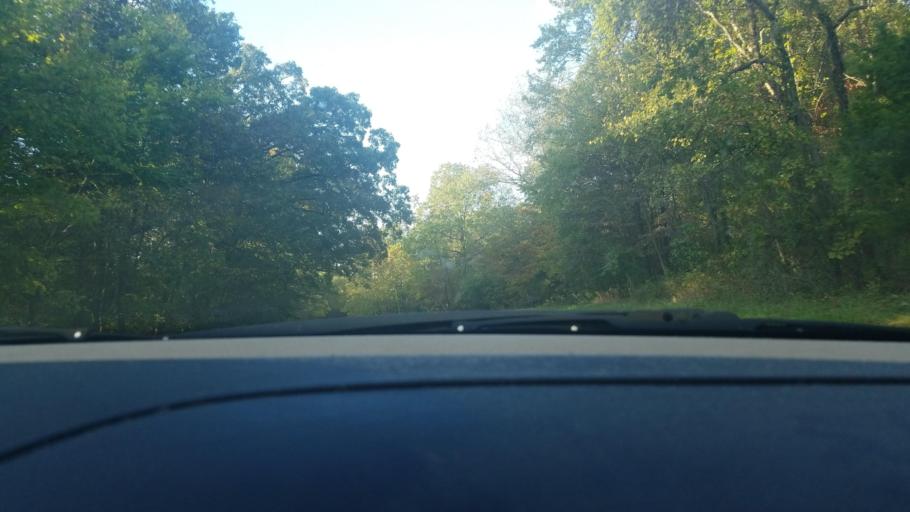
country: US
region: Illinois
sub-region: Saline County
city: Carrier Mills
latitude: 37.7738
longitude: -88.7143
